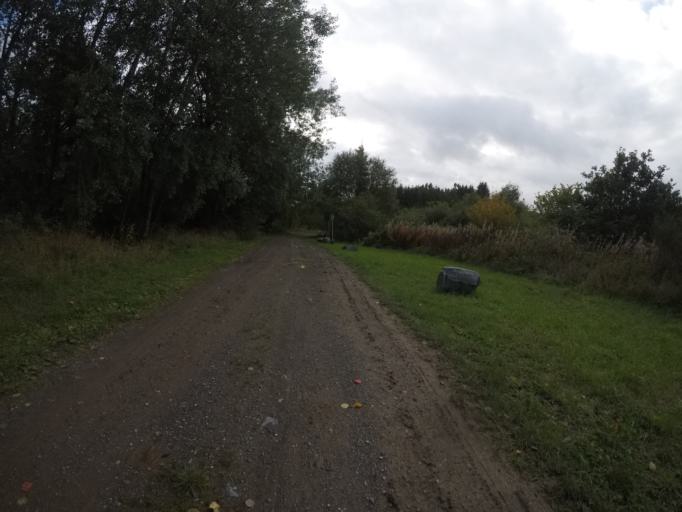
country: BE
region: Wallonia
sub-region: Province du Luxembourg
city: Fauvillers
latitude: 49.9162
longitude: 5.6914
